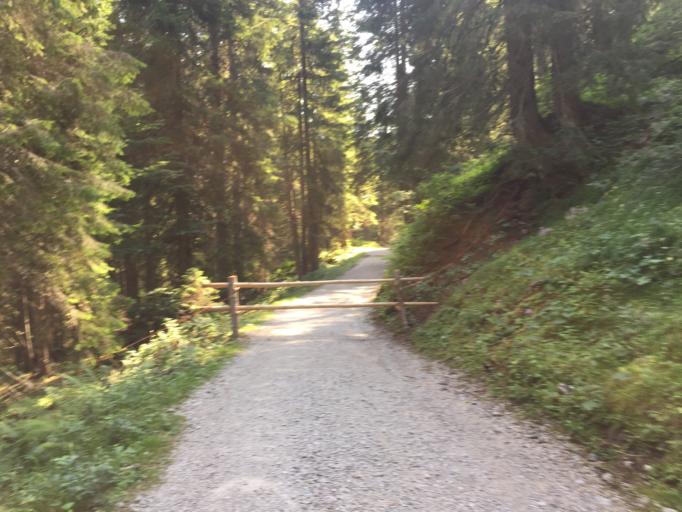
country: IT
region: Friuli Venezia Giulia
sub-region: Provincia di Udine
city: Forni Avoltri
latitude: 46.5610
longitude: 12.7570
